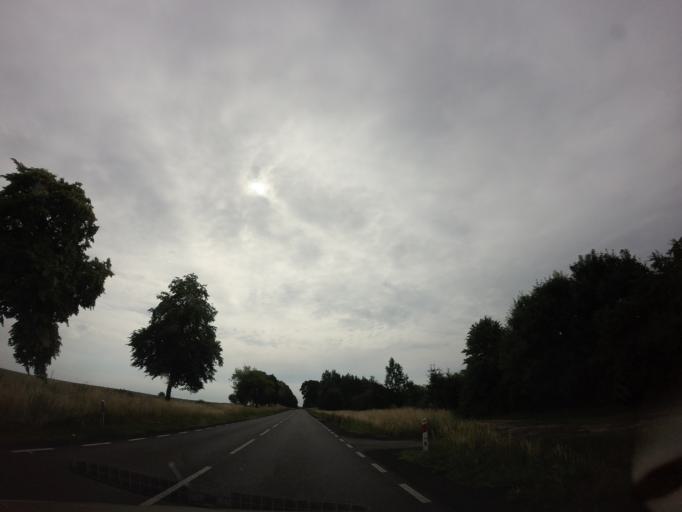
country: PL
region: West Pomeranian Voivodeship
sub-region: Powiat drawski
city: Kalisz Pomorski
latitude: 53.2969
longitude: 15.9246
